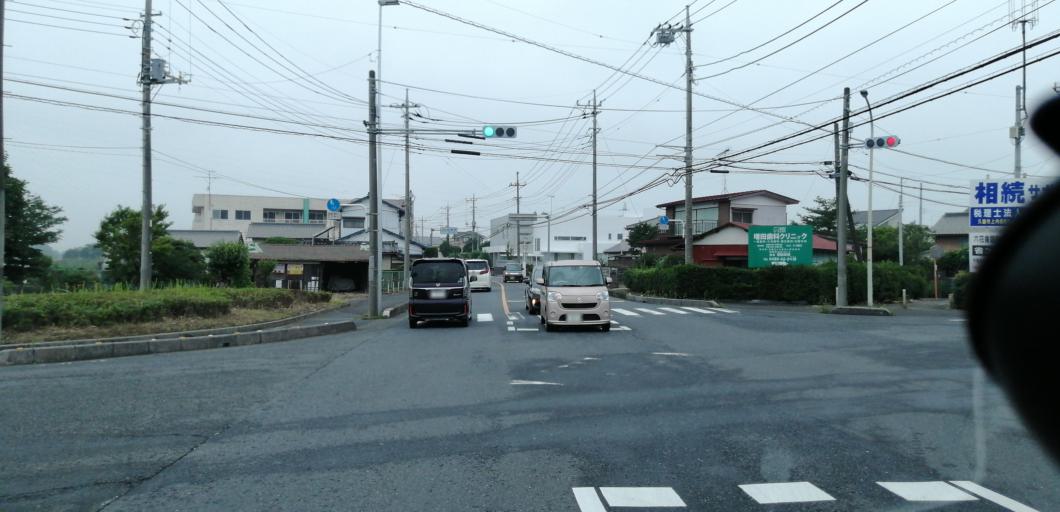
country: JP
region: Saitama
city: Kukichuo
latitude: 36.1050
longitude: 139.6579
